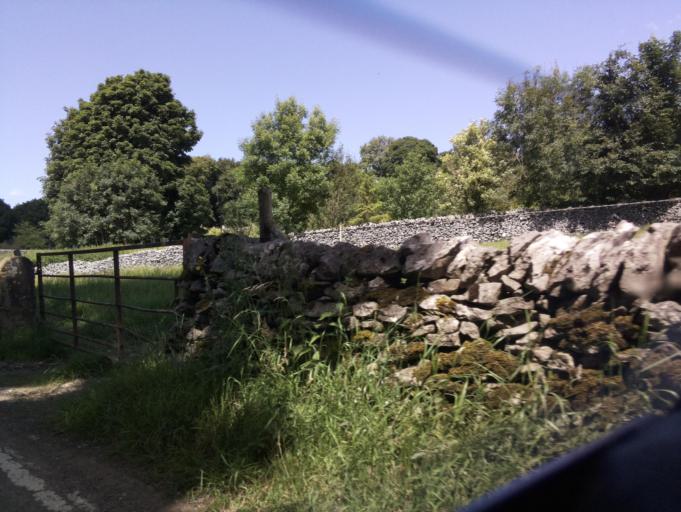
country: GB
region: England
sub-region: Derbyshire
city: Tideswell
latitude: 53.2616
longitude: -1.8133
